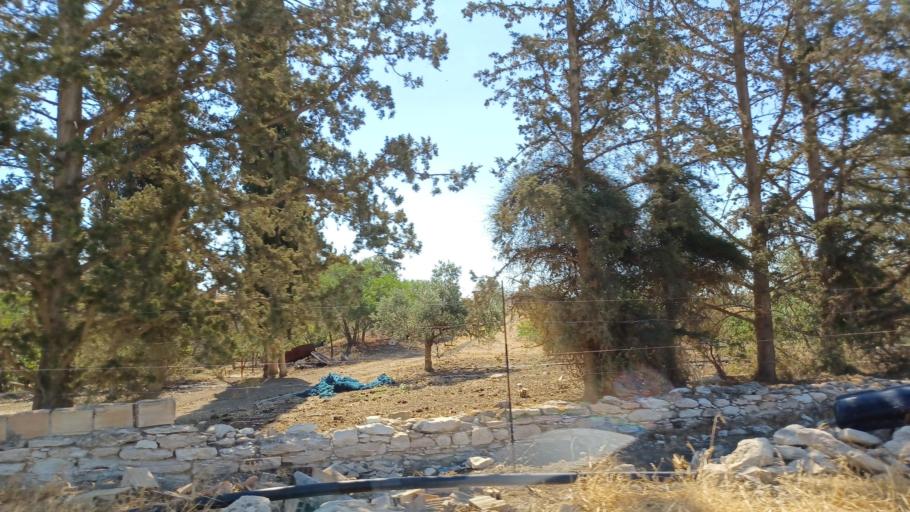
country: CY
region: Larnaka
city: Troulloi
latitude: 35.0102
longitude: 33.5862
